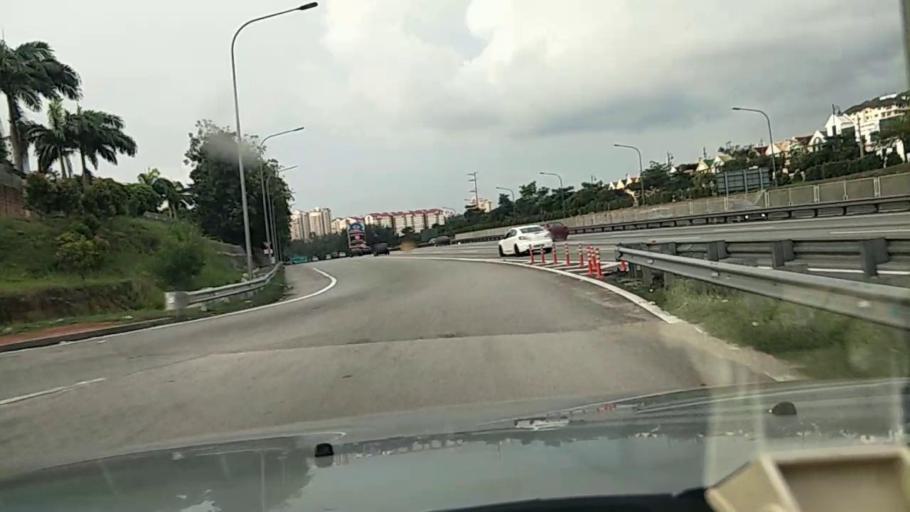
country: MY
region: Selangor
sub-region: Petaling
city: Petaling Jaya
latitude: 3.1232
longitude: 101.5944
